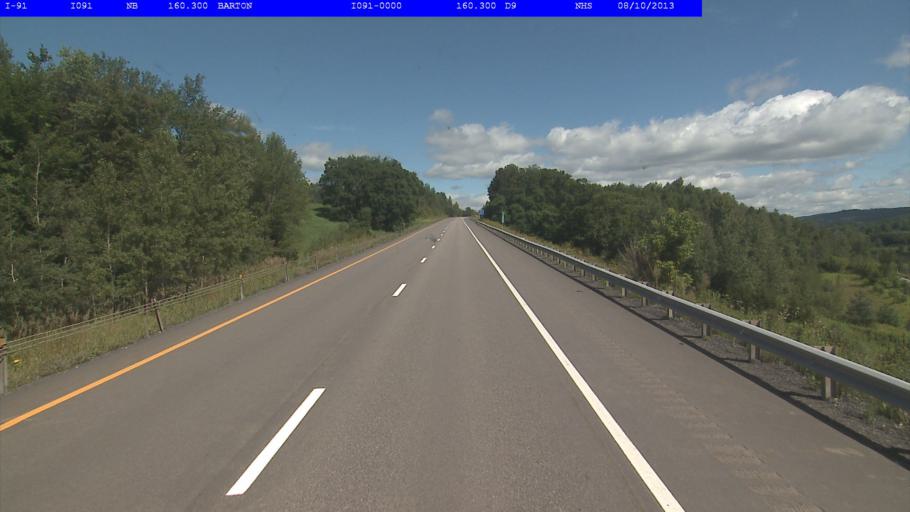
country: US
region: Vermont
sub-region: Orleans County
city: Newport
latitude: 44.7908
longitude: -72.2154
